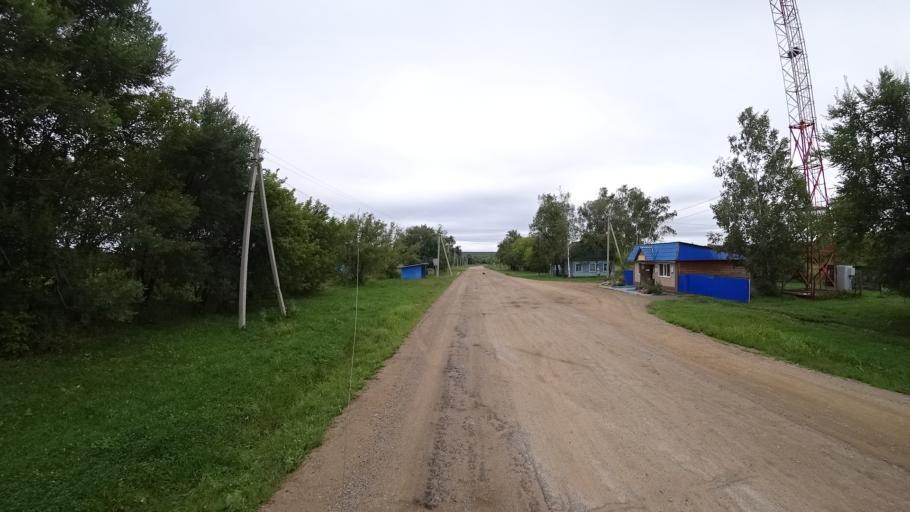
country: RU
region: Primorskiy
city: Rettikhovka
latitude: 44.1383
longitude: 132.6468
